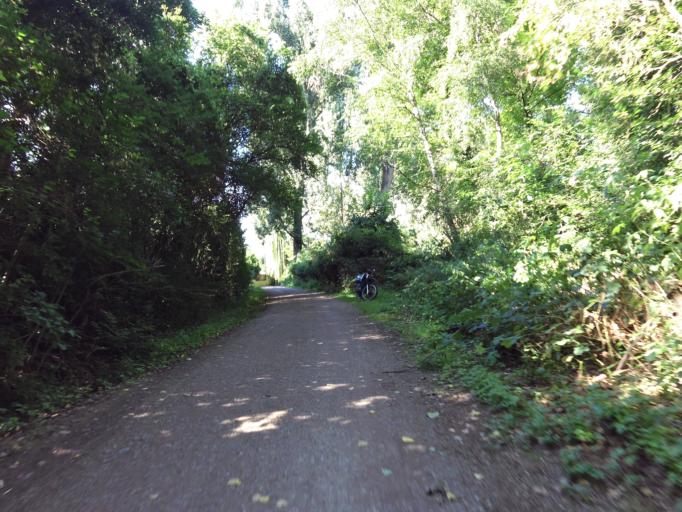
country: DE
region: Rheinland-Pfalz
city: Mutterstadt
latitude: 49.4710
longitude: 8.3648
